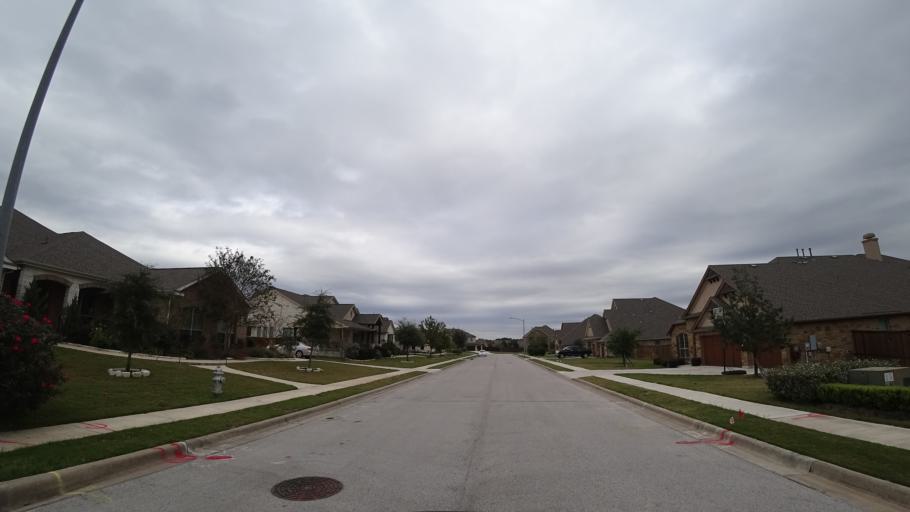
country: US
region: Texas
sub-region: Travis County
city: Shady Hollow
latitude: 30.1471
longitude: -97.8568
